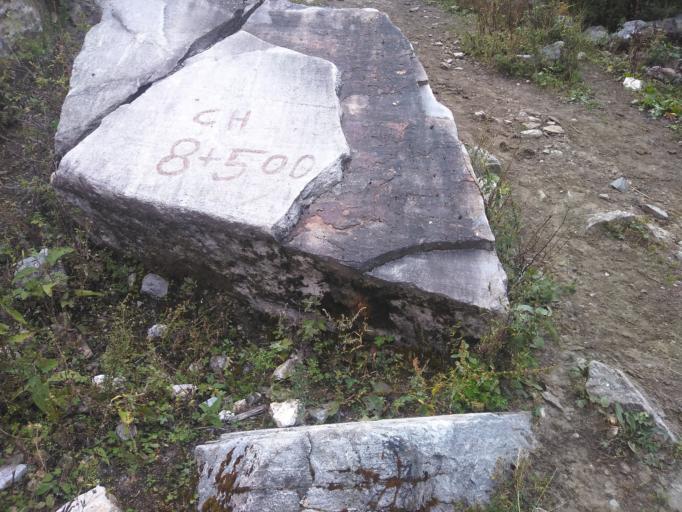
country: NP
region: Western Region
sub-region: Dhawalagiri Zone
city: Jomsom
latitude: 28.9275
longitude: 83.0406
